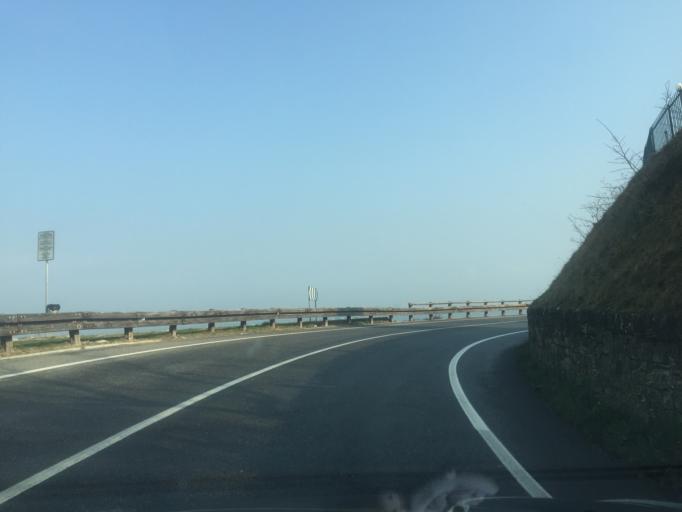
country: SI
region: Koper-Capodistria
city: Ankaran
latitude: 45.6056
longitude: 13.7193
